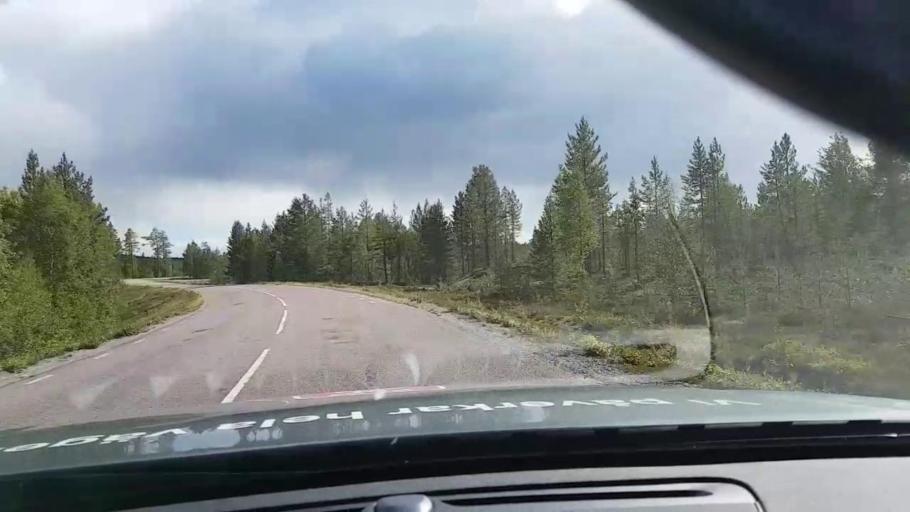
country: SE
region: Vaesterbotten
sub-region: Asele Kommun
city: Asele
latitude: 63.9035
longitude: 17.3450
